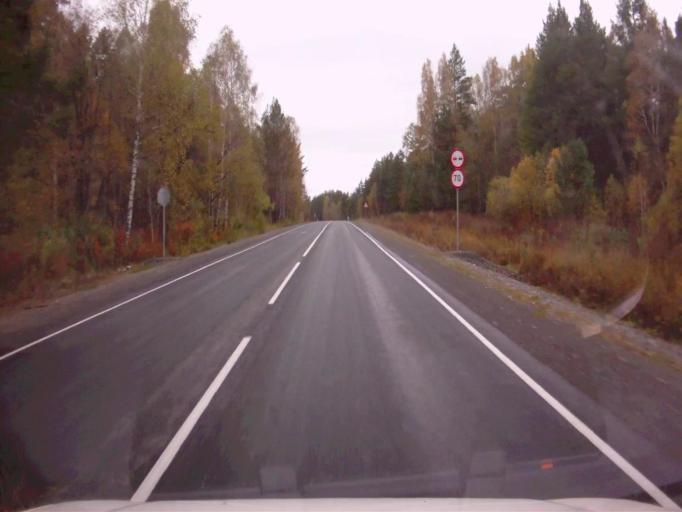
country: RU
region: Chelyabinsk
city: Nyazepetrovsk
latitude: 56.0592
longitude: 59.7321
